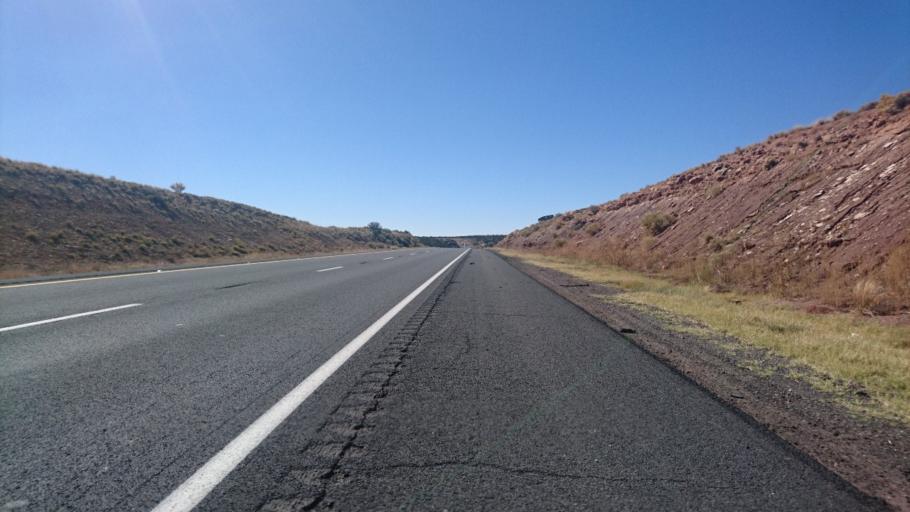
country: US
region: Arizona
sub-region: Apache County
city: Houck
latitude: 35.2785
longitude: -109.2528
